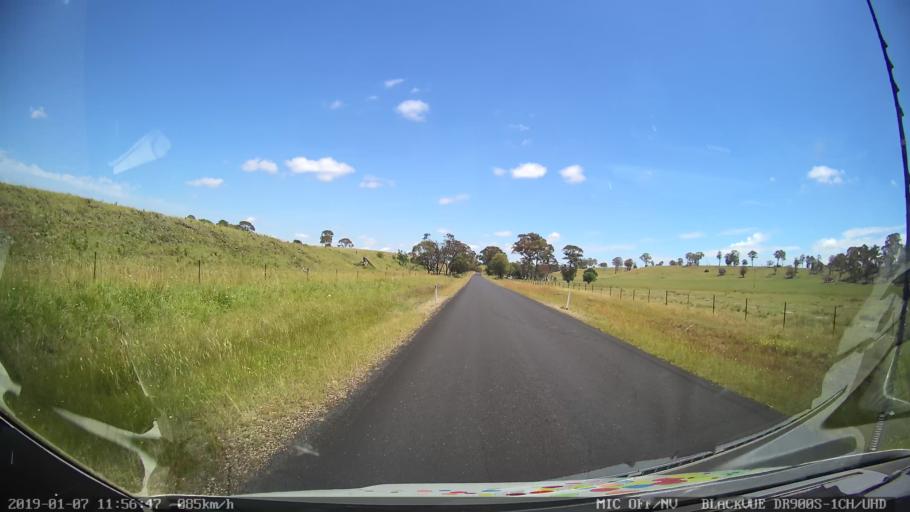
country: AU
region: New South Wales
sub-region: Guyra
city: Guyra
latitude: -30.2710
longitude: 151.6708
